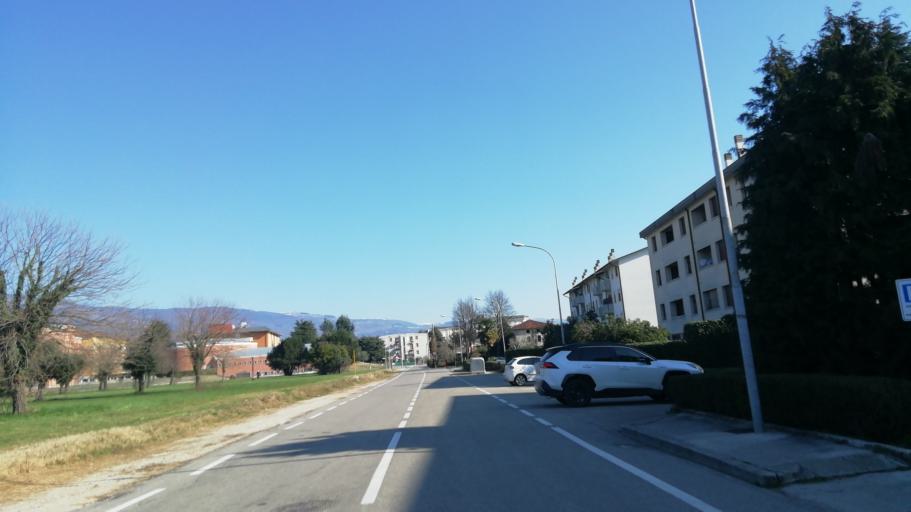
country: IT
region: Veneto
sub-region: Provincia di Vicenza
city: Thiene
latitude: 45.7075
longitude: 11.4645
